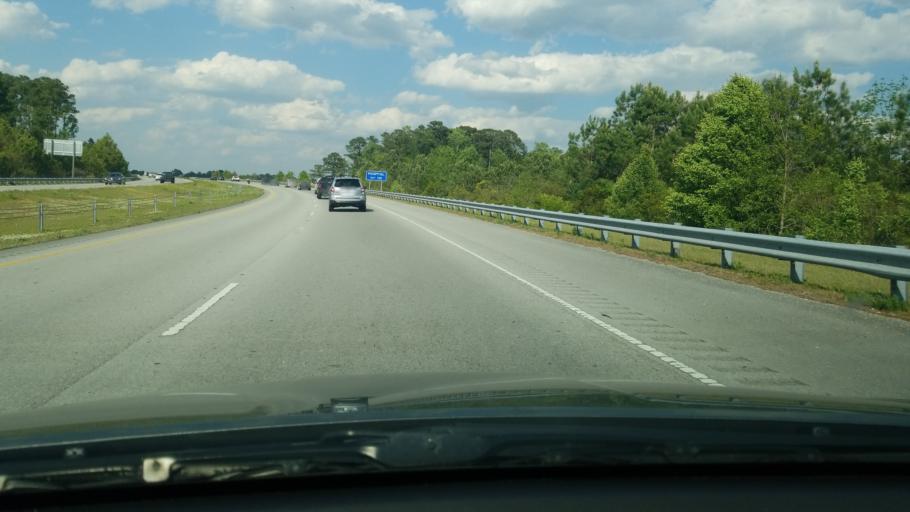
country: US
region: North Carolina
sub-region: Onslow County
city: Jacksonville
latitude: 34.7522
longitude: -77.3982
